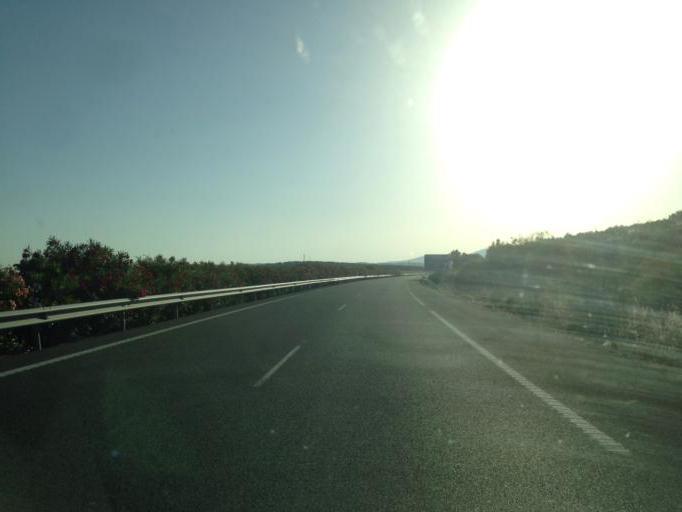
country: ES
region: Andalusia
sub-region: Provincia de Malaga
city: Villanueva del Trabuco
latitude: 37.0623
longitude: -4.3454
